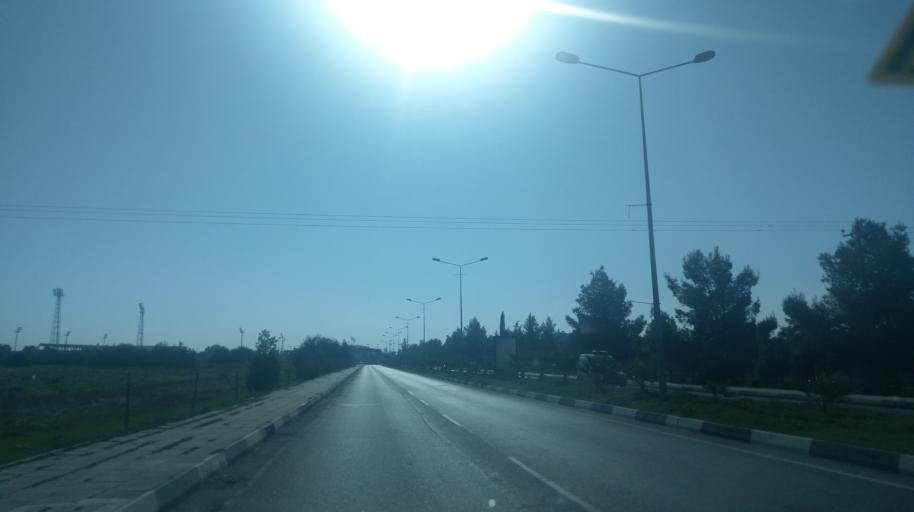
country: CY
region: Lefkosia
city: Nicosia
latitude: 35.2166
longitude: 33.3325
